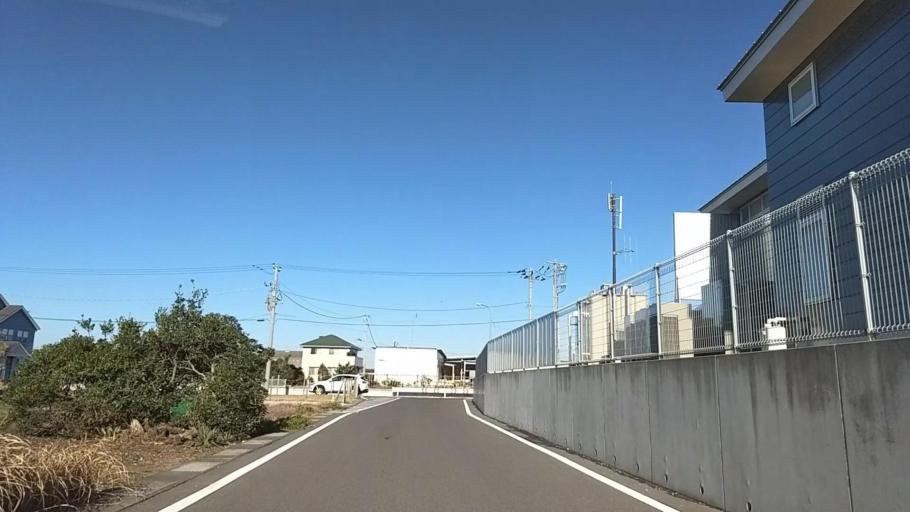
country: JP
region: Chiba
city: Naruto
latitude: 35.5385
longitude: 140.4571
